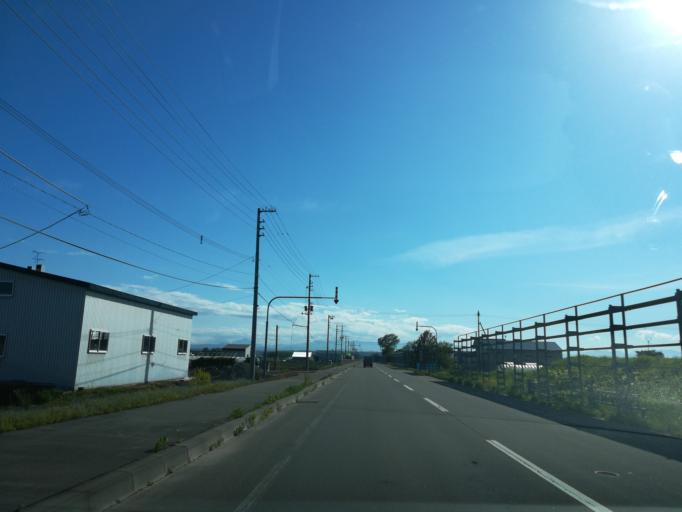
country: JP
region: Hokkaido
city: Ebetsu
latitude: 43.0546
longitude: 141.6118
